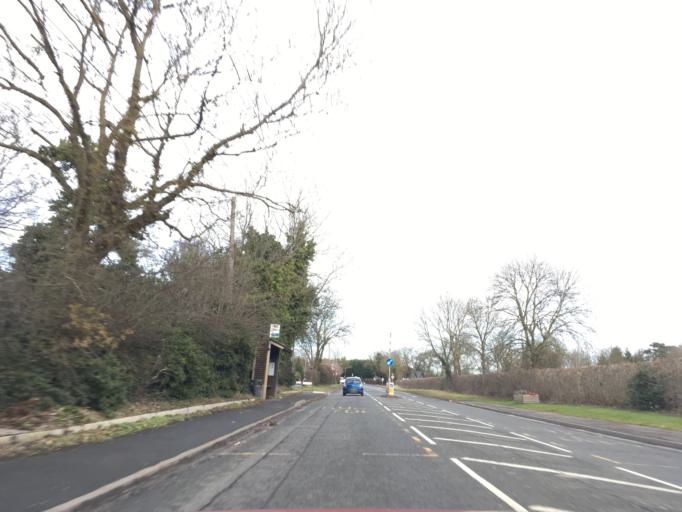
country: GB
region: England
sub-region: Nottinghamshire
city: Ruddington
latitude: 52.8645
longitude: -1.1325
